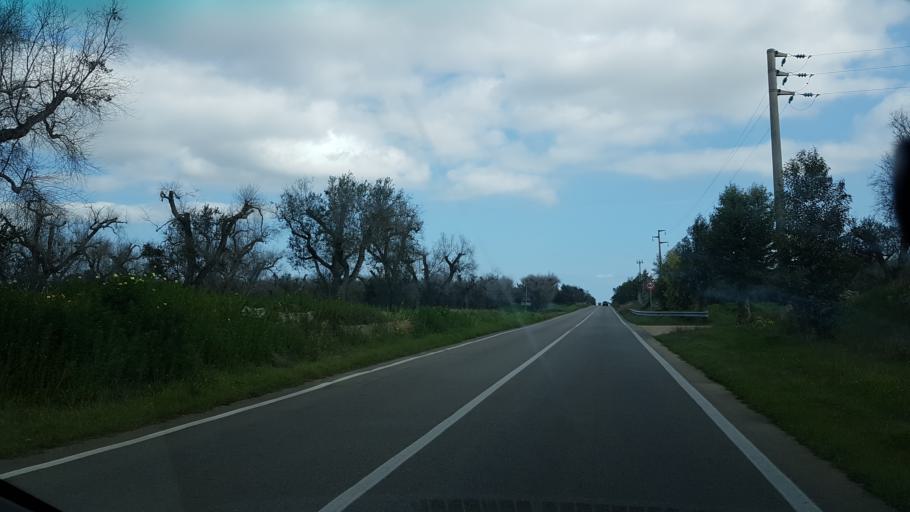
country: IT
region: Apulia
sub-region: Provincia di Brindisi
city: Torchiarolo
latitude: 40.4583
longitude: 18.0664
